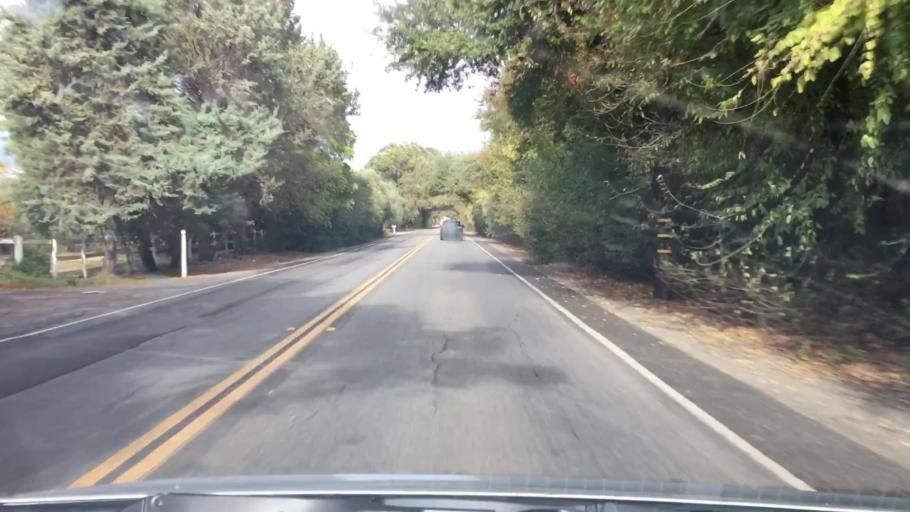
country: US
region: California
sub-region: Yolo County
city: Davis
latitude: 38.5496
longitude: -121.8033
